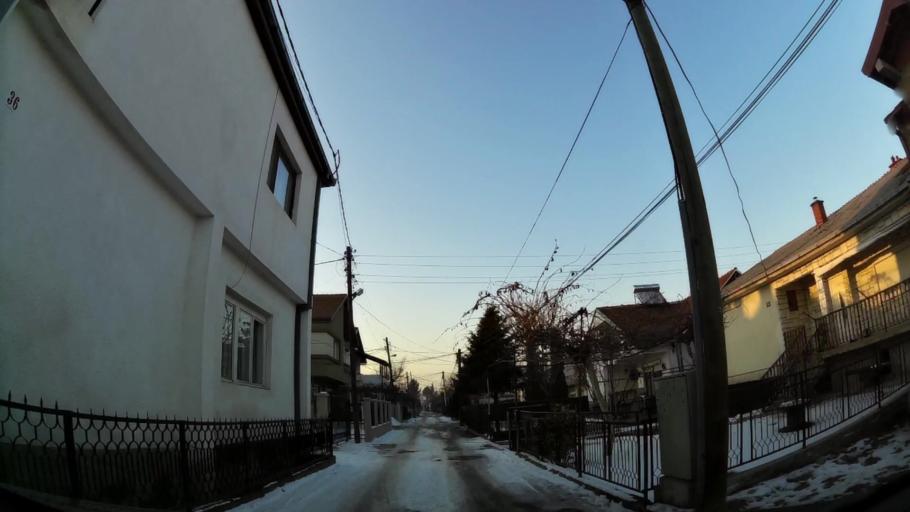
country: MK
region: Kisela Voda
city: Kisela Voda
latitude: 41.9786
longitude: 21.4907
